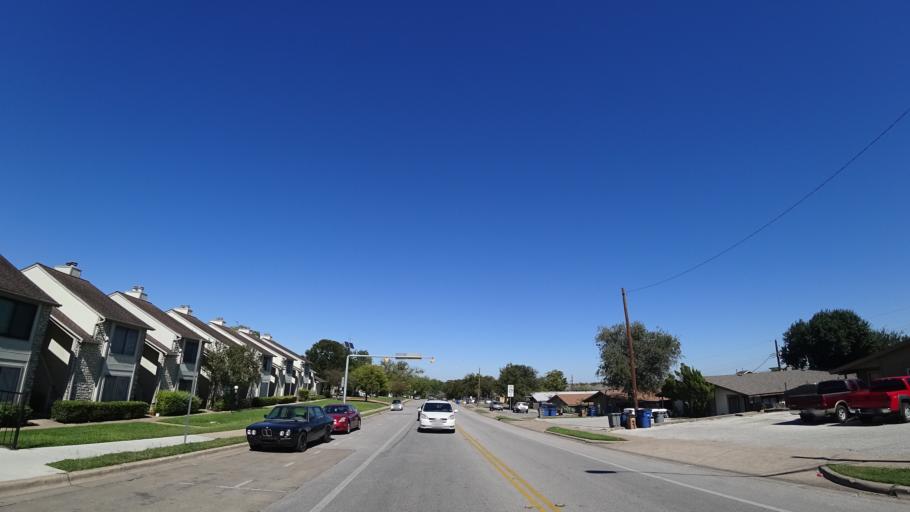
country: US
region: Texas
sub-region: Travis County
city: Austin
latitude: 30.2249
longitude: -97.7420
